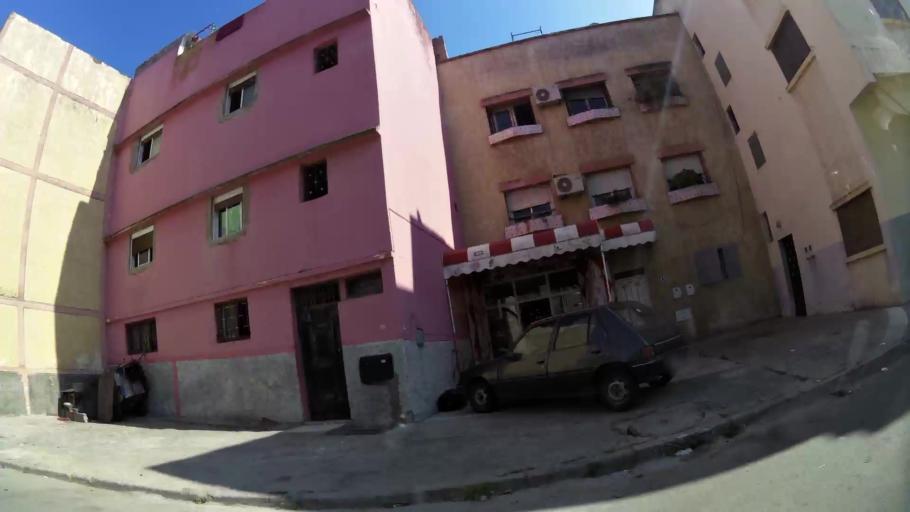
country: MA
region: Rabat-Sale-Zemmour-Zaer
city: Sale
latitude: 34.0418
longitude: -6.7836
